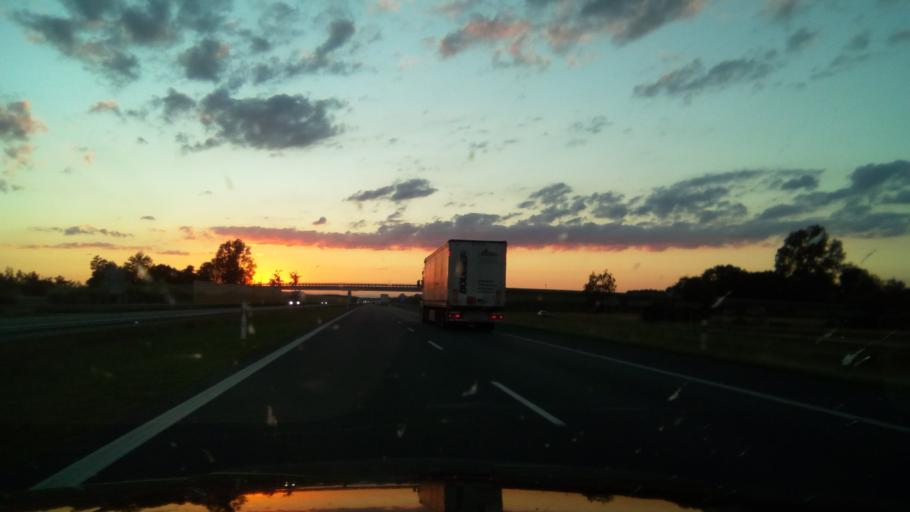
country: PL
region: Greater Poland Voivodeship
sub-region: Powiat kolski
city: Dabie
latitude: 52.0466
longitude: 18.8542
